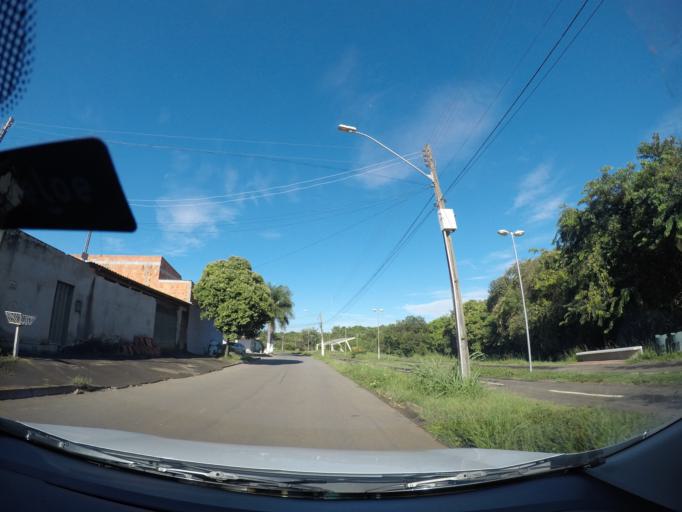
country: BR
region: Goias
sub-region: Goiania
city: Goiania
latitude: -16.7383
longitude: -49.3168
